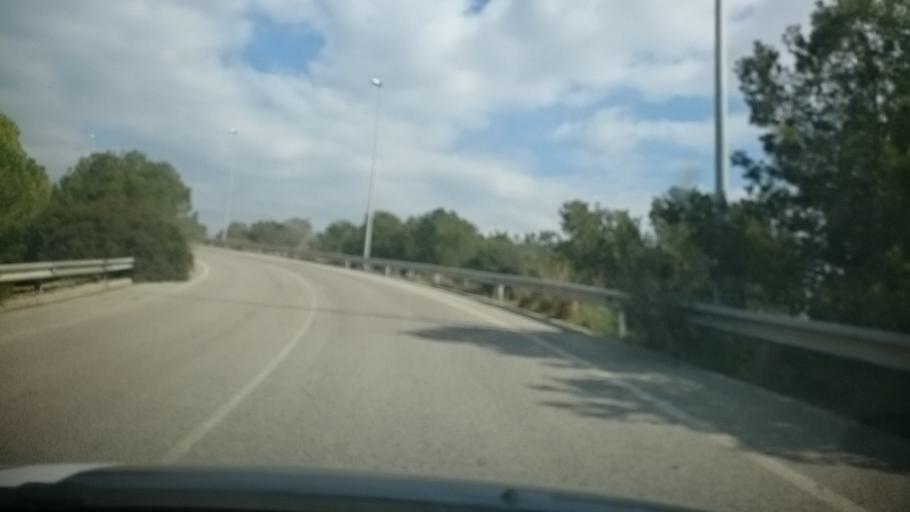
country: ES
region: Catalonia
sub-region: Provincia de Barcelona
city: Cubelles
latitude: 41.2073
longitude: 1.6591
